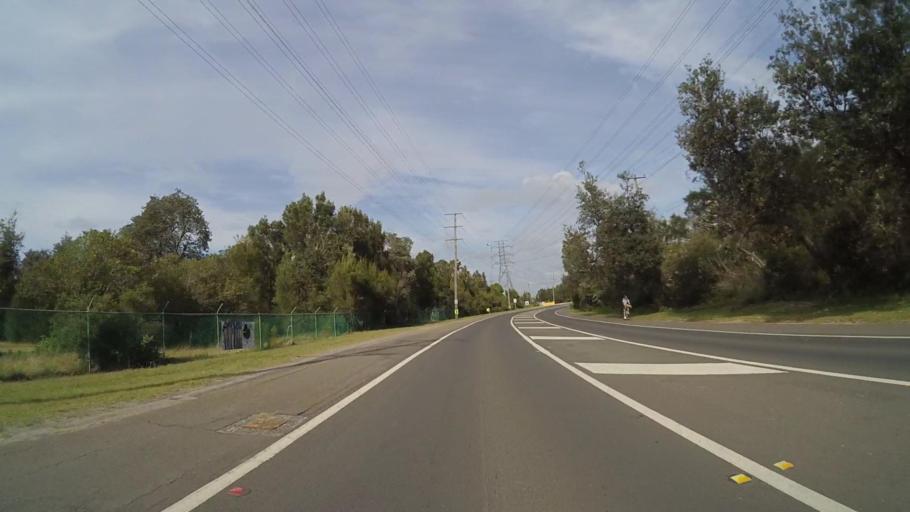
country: AU
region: New South Wales
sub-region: Sutherland Shire
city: Kurnell
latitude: -34.0221
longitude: 151.1972
